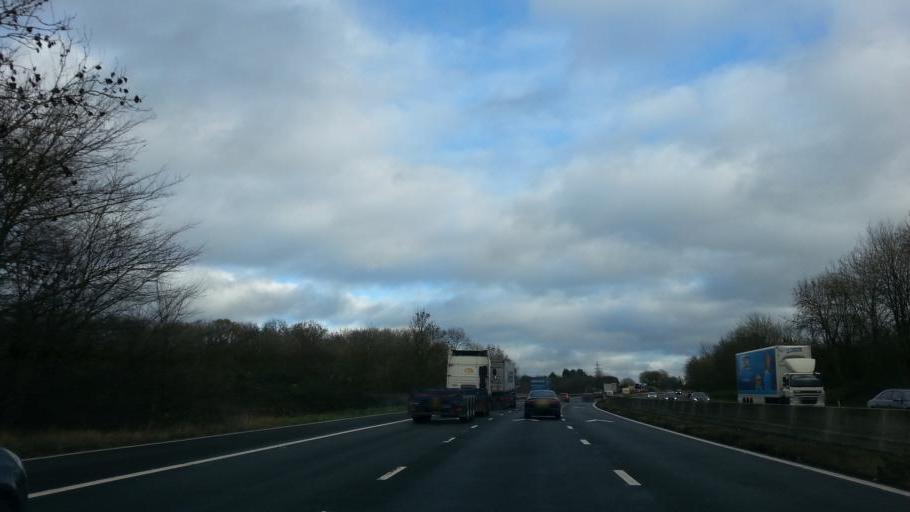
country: GB
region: England
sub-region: Wiltshire
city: Royal Wootton Bassett
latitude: 51.5593
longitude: -1.9122
